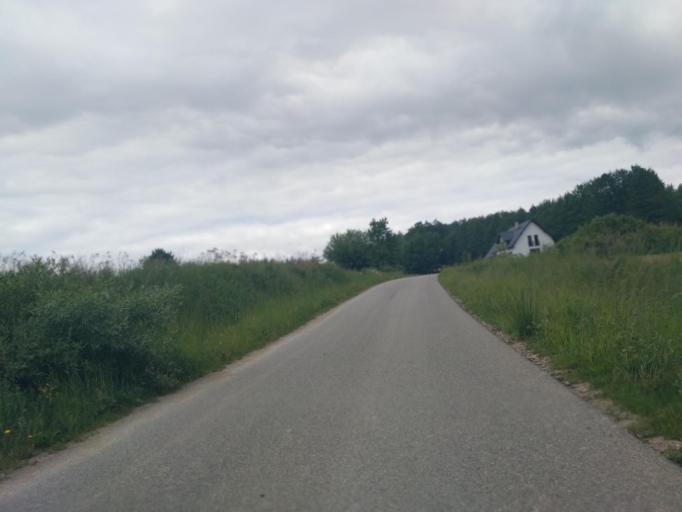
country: PL
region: Subcarpathian Voivodeship
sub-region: Powiat jasielski
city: Tarnowiec
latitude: 49.6924
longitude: 21.5806
